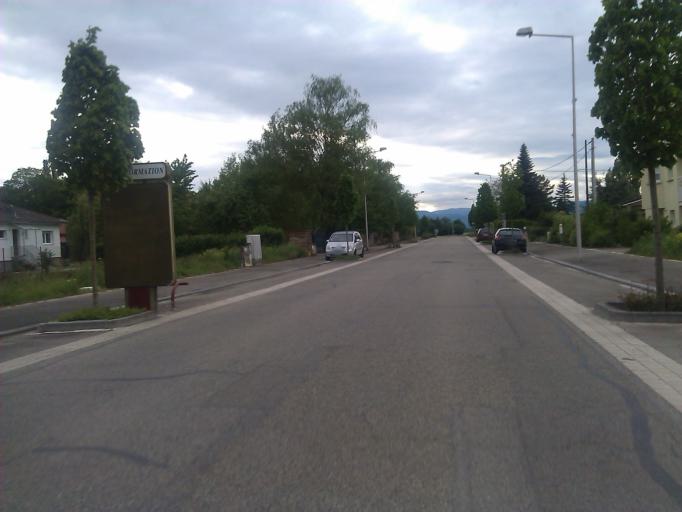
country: FR
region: Alsace
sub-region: Departement du Bas-Rhin
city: Marckolsheim
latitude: 48.1604
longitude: 7.5308
